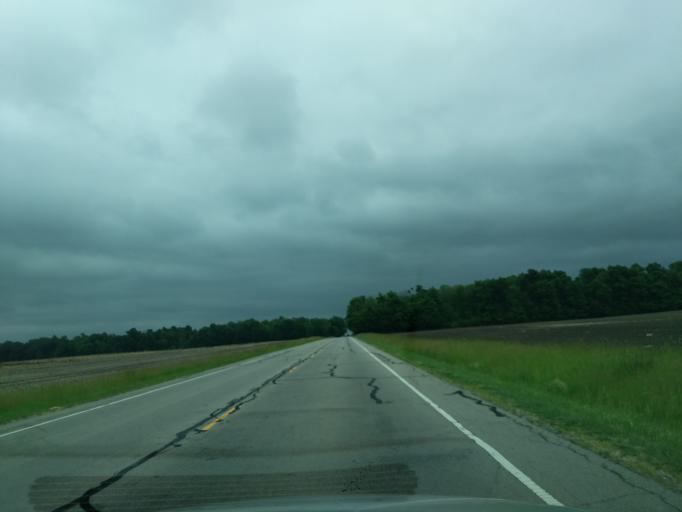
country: US
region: Indiana
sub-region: Madison County
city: Alexandria
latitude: 40.2772
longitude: -85.6083
